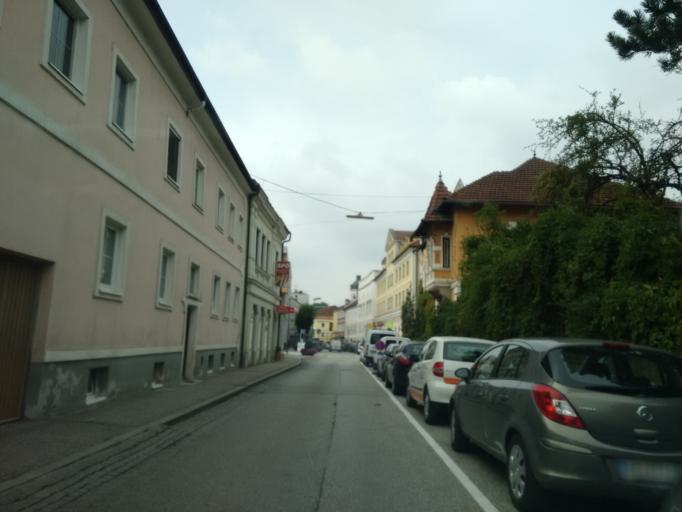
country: AT
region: Upper Austria
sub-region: Politischer Bezirk Grieskirchen
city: Grieskirchen
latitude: 48.2341
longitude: 13.8336
